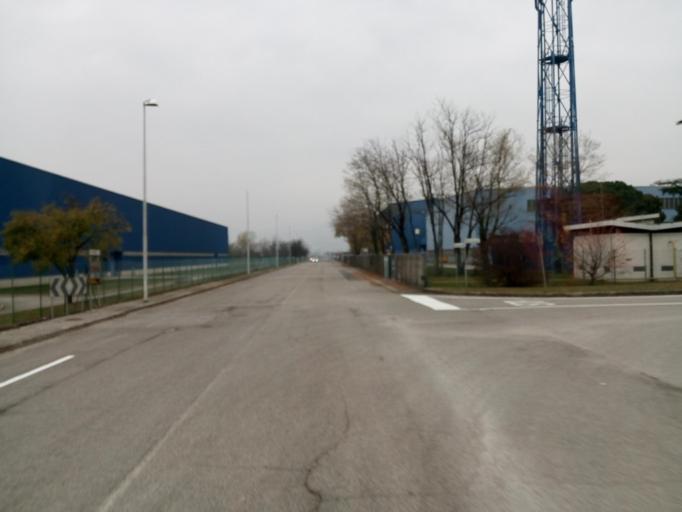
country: IT
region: Friuli Venezia Giulia
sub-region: Provincia di Udine
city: Moimacco
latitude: 46.0865
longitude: 13.3909
